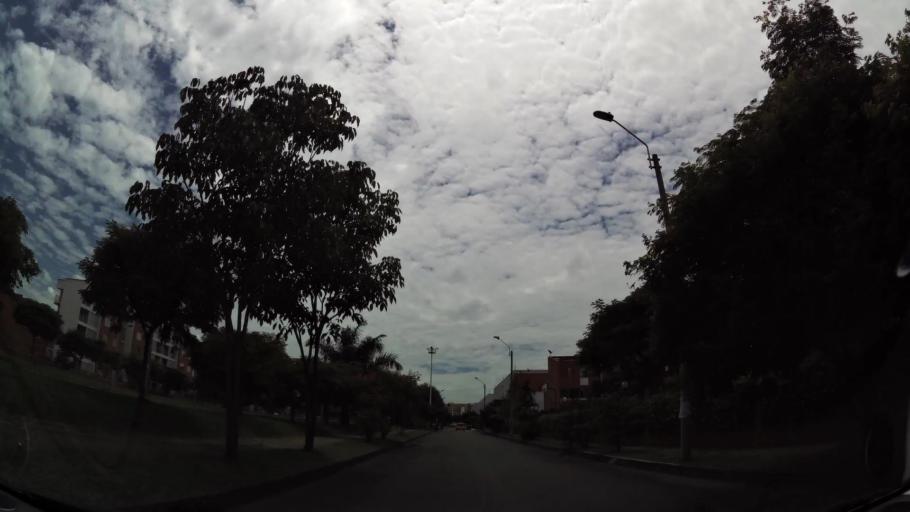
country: CO
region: Valle del Cauca
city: Cali
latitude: 3.3704
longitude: -76.5225
